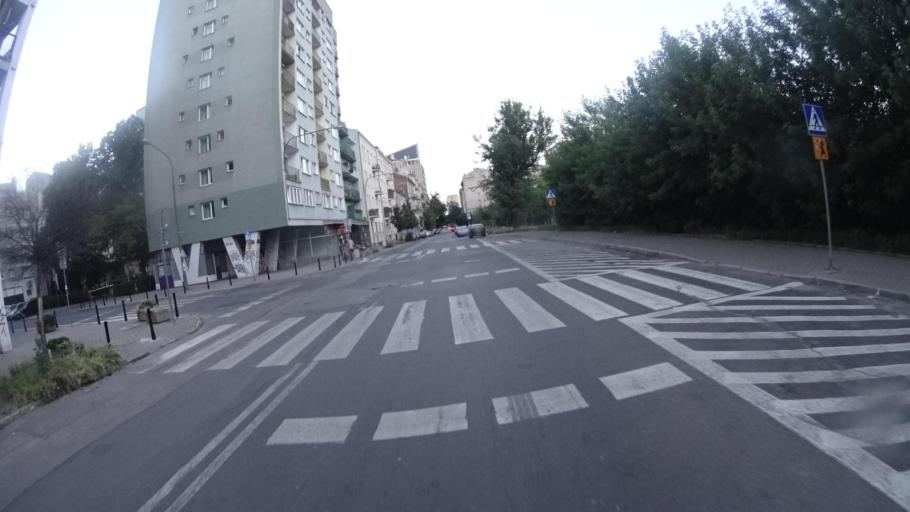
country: PL
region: Masovian Voivodeship
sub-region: Warszawa
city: Ochota
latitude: 52.2299
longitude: 20.9902
